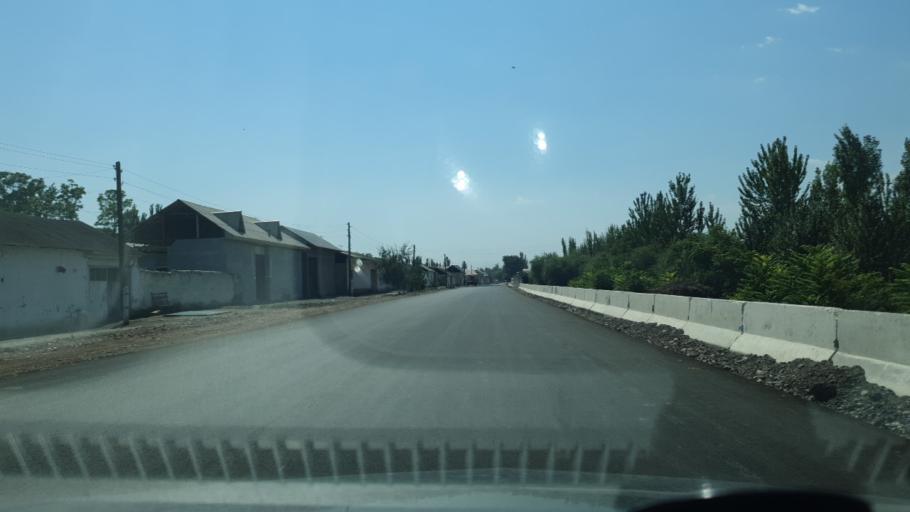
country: UZ
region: Namangan
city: Pop
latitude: 40.6341
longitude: 71.1934
